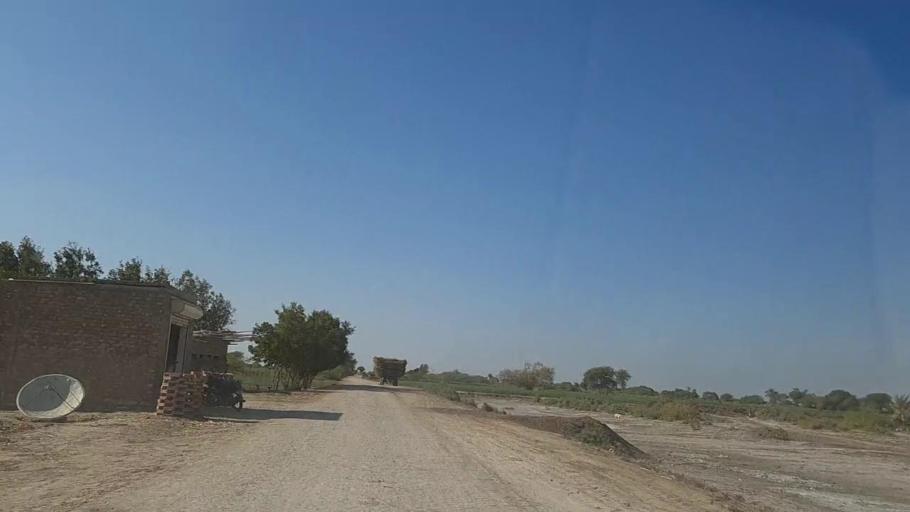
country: PK
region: Sindh
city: Digri
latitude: 25.1793
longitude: 69.0098
